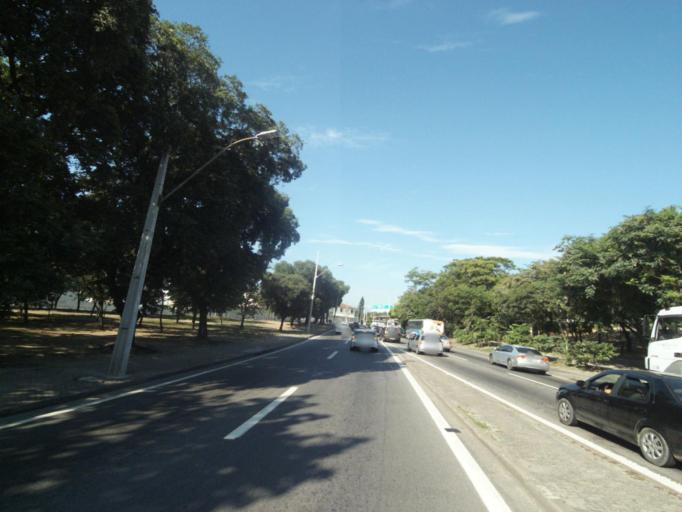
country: BR
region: Rio de Janeiro
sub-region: Niteroi
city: Niteroi
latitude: -22.8815
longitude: -43.1136
